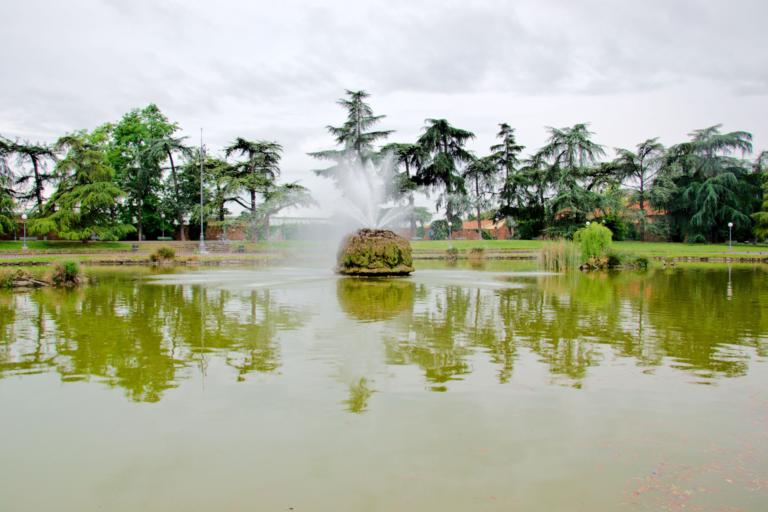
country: IT
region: Tuscany
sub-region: Province of Florence
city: Florence
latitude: 43.7825
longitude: 11.2512
